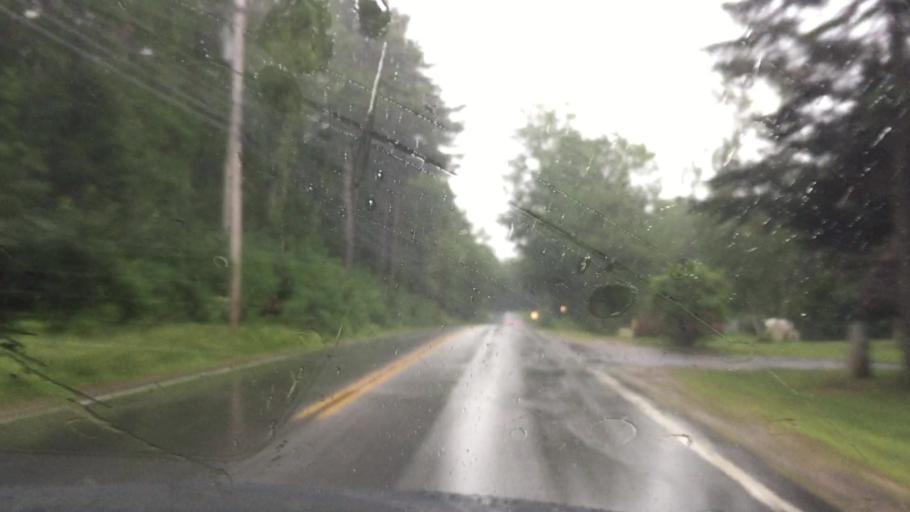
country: US
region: New Hampshire
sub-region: Belknap County
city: Meredith
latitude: 43.6964
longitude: -71.5161
